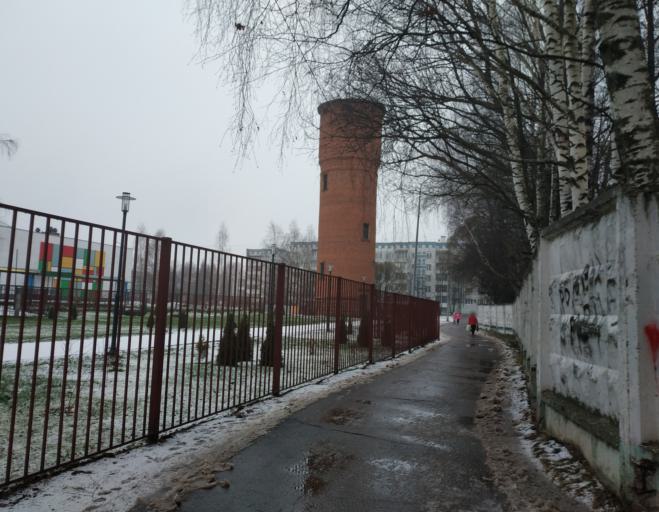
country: RU
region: Moskovskaya
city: Taldom
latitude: 56.7418
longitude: 37.5342
